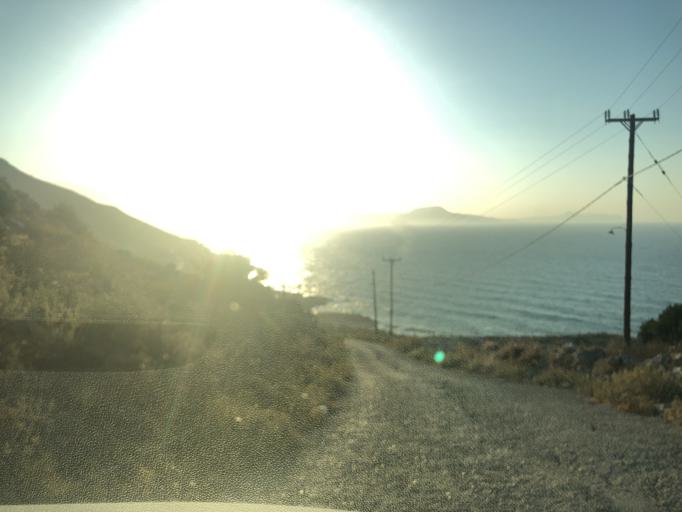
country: GR
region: Crete
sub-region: Nomos Rethymnis
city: Atsipopoulon
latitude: 35.3586
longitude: 24.3959
